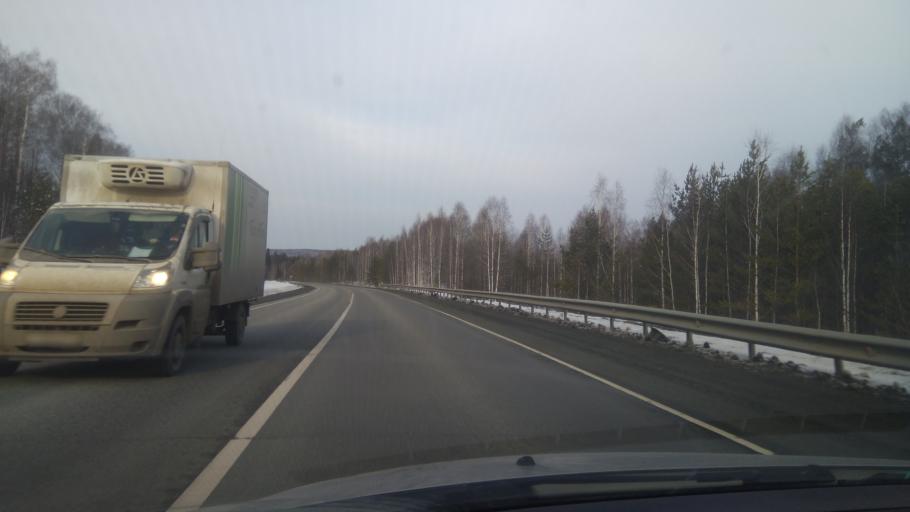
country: RU
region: Sverdlovsk
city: Bisert'
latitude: 56.8372
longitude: 58.8767
